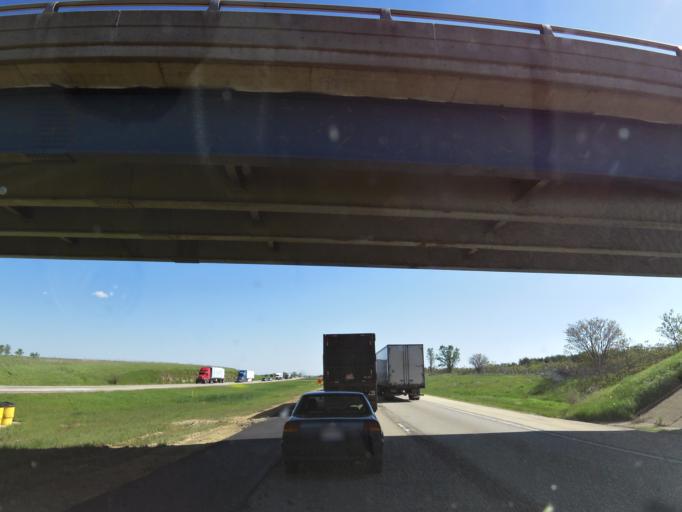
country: US
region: Illinois
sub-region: Ogle County
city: Davis Junction
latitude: 42.0435
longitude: -89.0210
